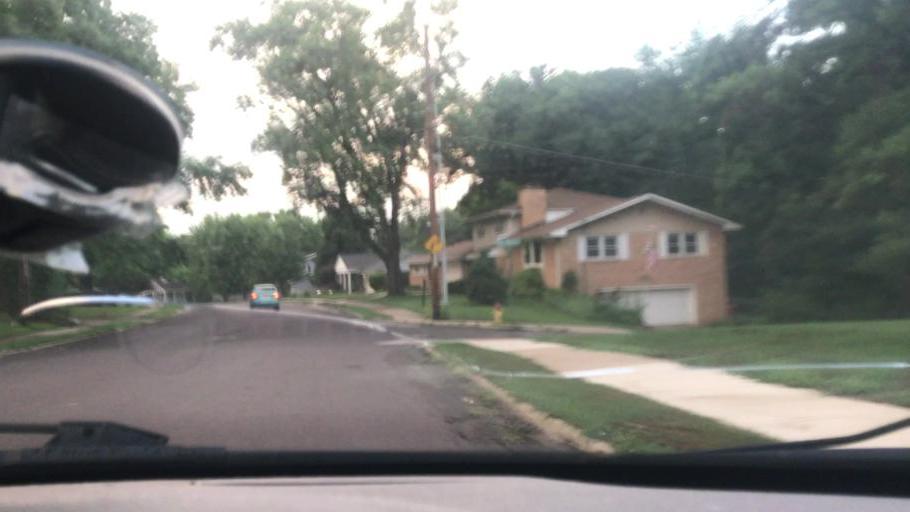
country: US
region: Illinois
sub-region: Tazewell County
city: Pekin
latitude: 40.5455
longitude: -89.6157
